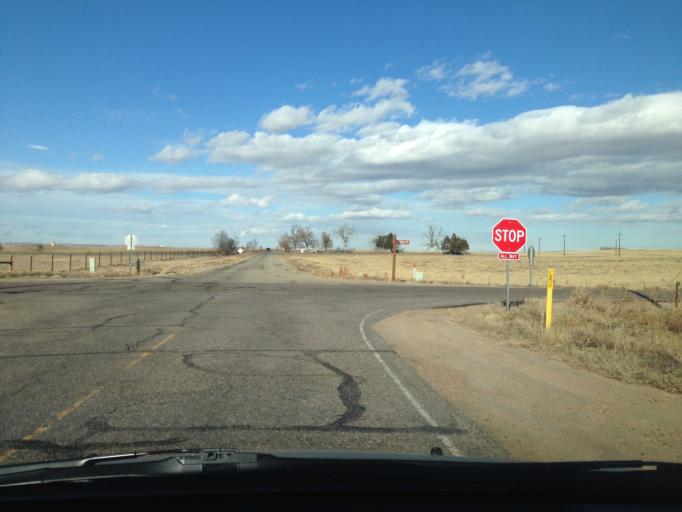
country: US
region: Colorado
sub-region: Adams County
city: Derby
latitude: 39.8270
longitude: -104.8656
